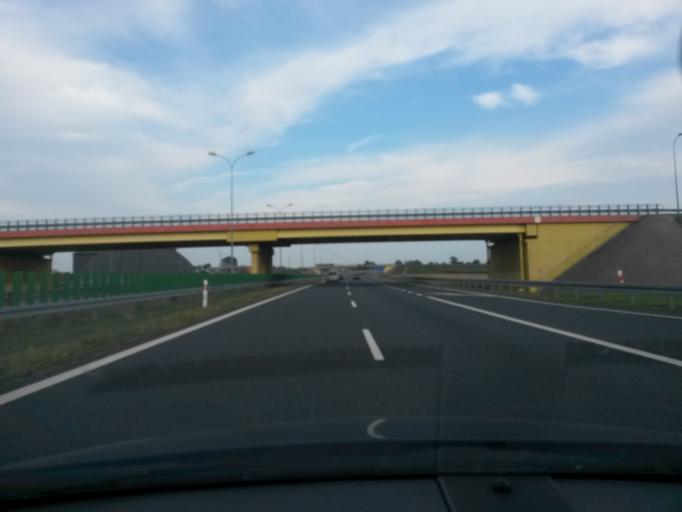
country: PL
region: Lodz Voivodeship
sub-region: Powiat poddebicki
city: Wartkowice
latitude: 51.9948
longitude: 19.0387
